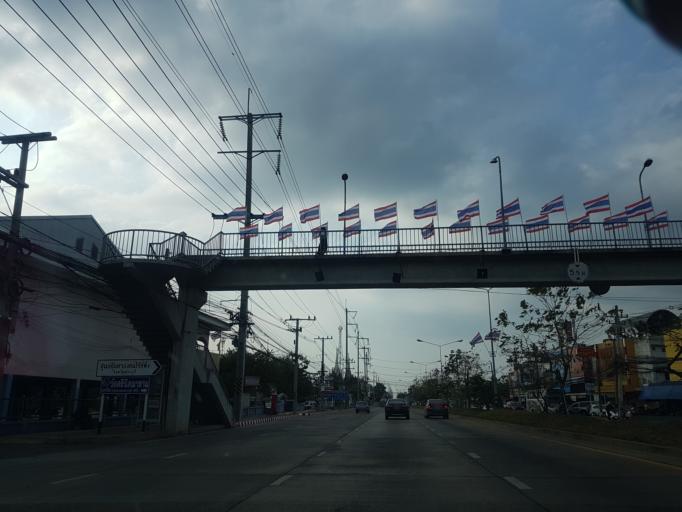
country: TH
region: Sara Buri
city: Phra Phutthabat
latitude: 14.7258
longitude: 100.7962
